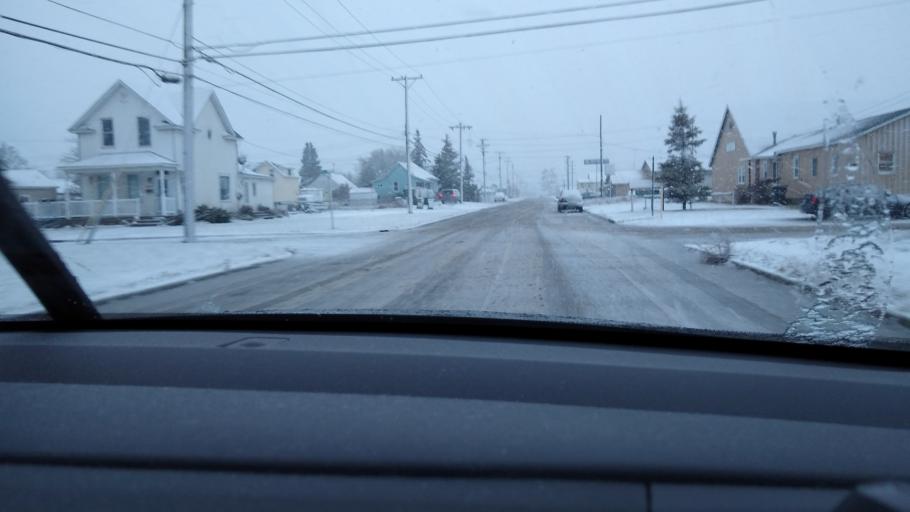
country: US
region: Michigan
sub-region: Delta County
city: Escanaba
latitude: 45.7536
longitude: -87.0729
